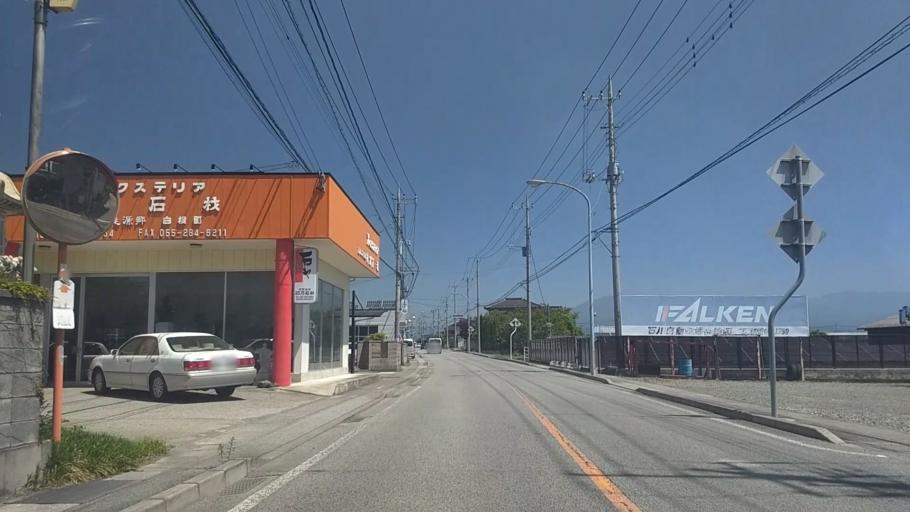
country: JP
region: Yamanashi
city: Ryuo
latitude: 35.6450
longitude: 138.4636
